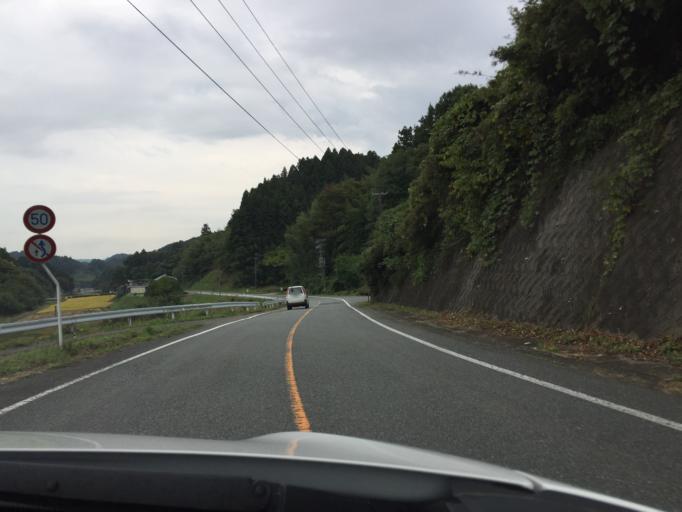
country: JP
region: Fukushima
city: Nihommatsu
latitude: 37.6031
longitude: 140.5362
